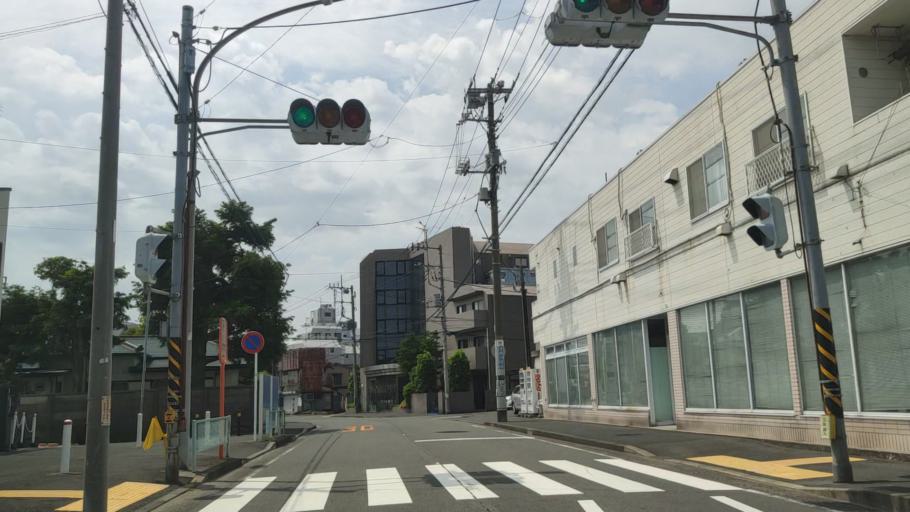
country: JP
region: Kanagawa
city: Yokohama
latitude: 35.4148
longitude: 139.6241
